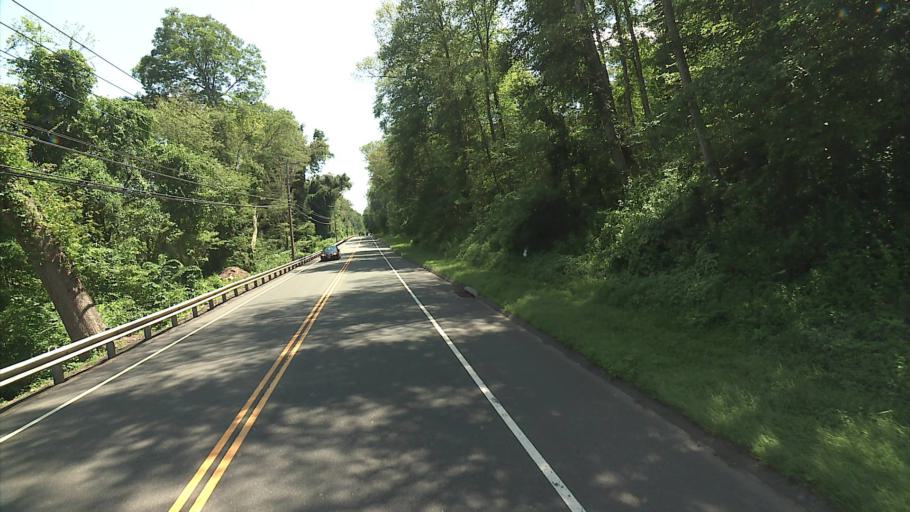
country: US
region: Connecticut
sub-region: Middlesex County
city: East Haddam
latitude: 41.4356
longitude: -72.4584
